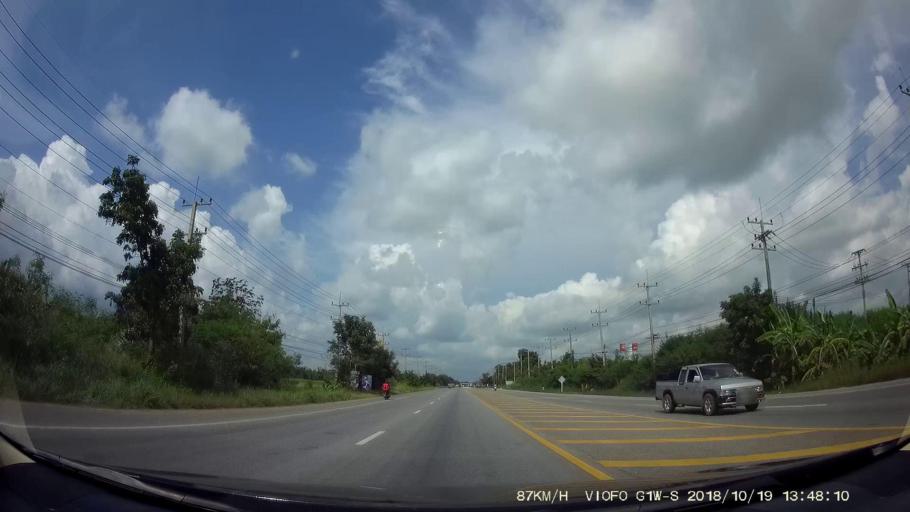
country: TH
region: Chaiyaphum
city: Chaiyaphum
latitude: 15.7227
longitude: 102.0174
